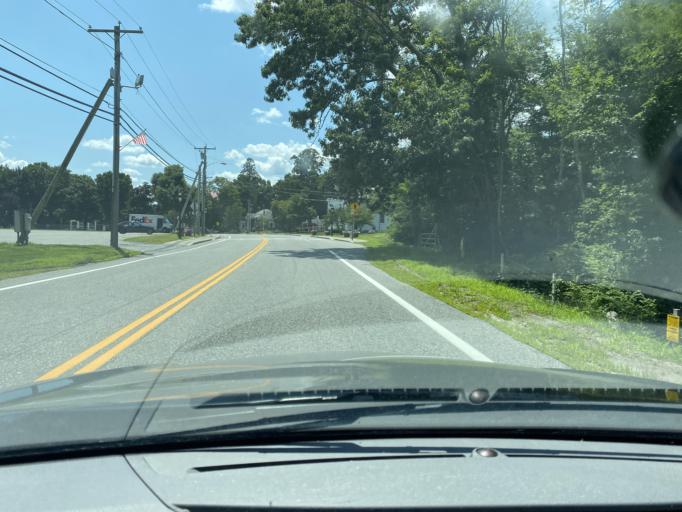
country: US
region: Rhode Island
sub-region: Providence County
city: North Scituate
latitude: 41.8353
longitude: -71.5860
